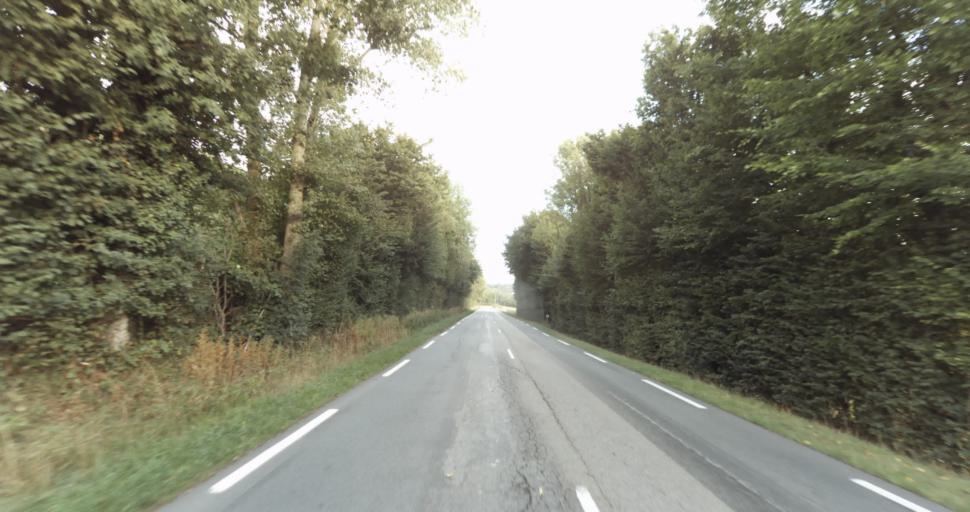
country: FR
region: Lower Normandy
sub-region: Departement de l'Orne
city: Sainte-Gauburge-Sainte-Colombe
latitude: 48.7234
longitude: 0.4203
